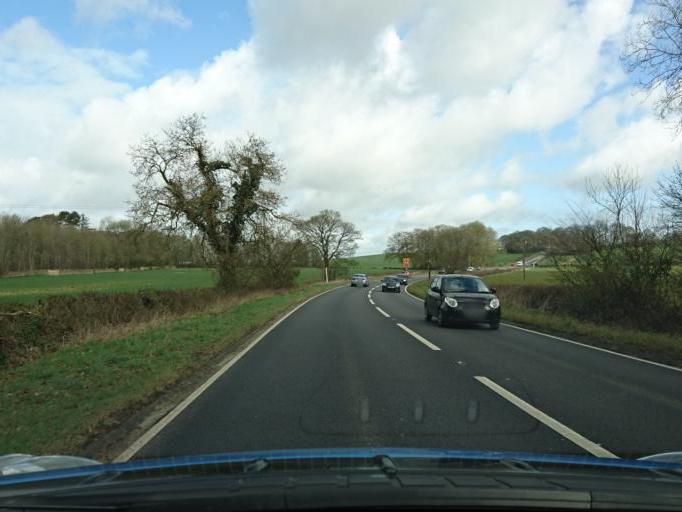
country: GB
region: England
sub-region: South Gloucestershire
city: Hinton
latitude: 51.4831
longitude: -2.3622
